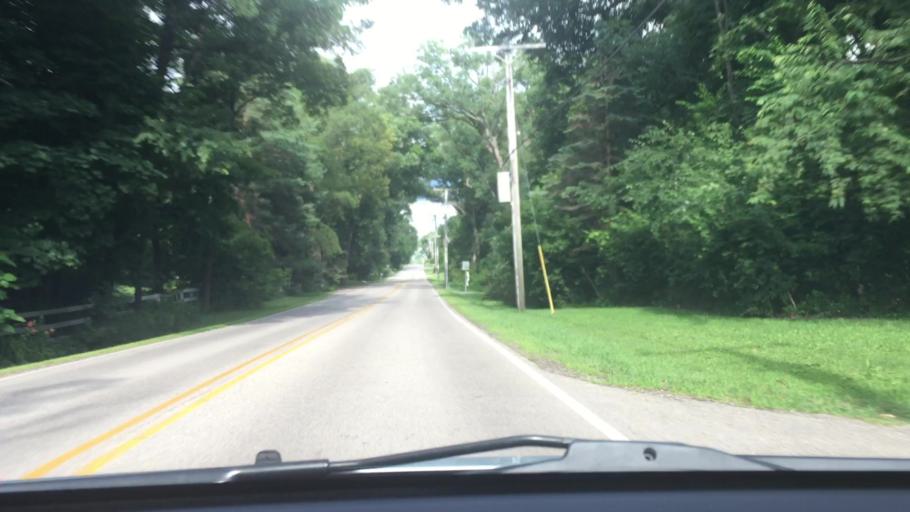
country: US
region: Illinois
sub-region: McHenry County
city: Crystal Lake
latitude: 42.2626
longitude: -88.3309
